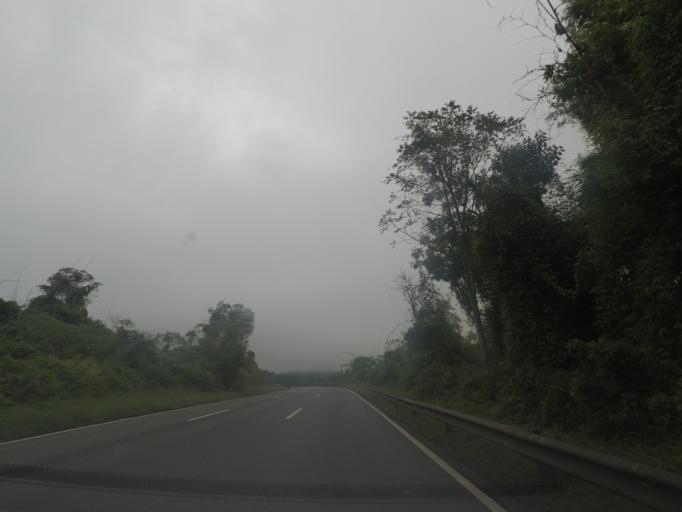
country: BR
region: Parana
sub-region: Antonina
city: Antonina
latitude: -25.0379
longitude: -48.5476
